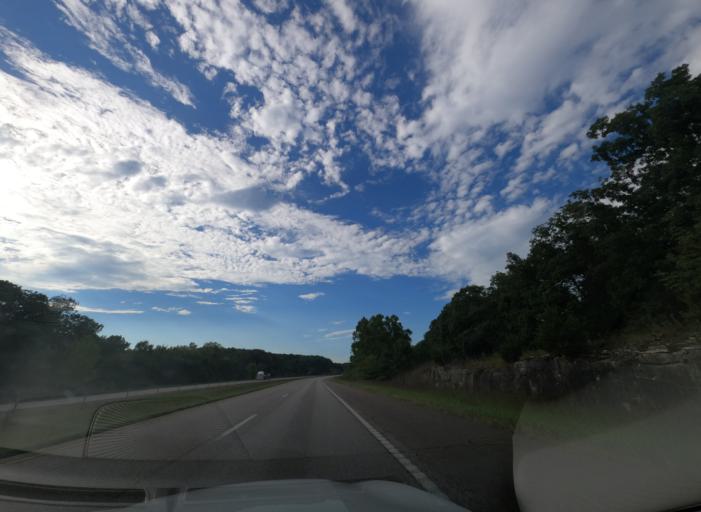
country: US
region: Missouri
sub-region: Jefferson County
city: Crystal City
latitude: 38.0701
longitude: -90.2902
